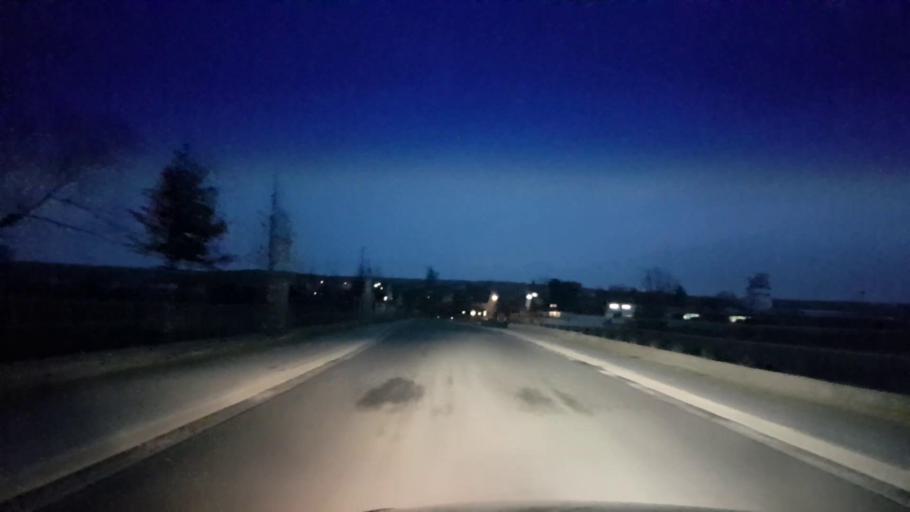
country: DE
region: Bavaria
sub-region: Upper Franconia
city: Burgebrach
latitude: 49.8347
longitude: 10.7619
